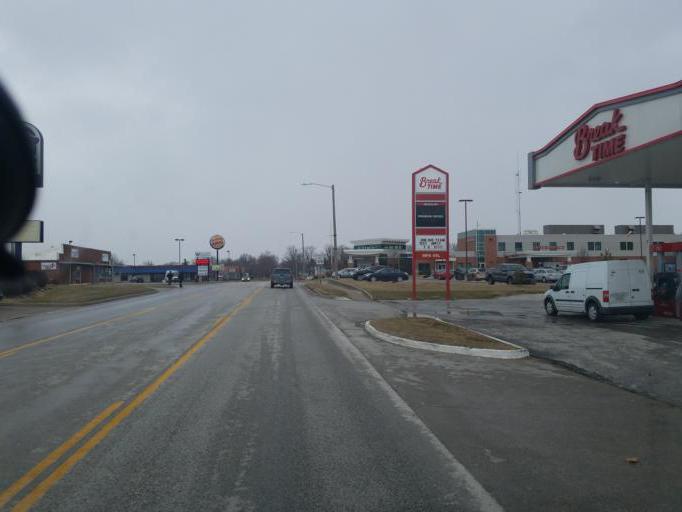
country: US
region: Missouri
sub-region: Macon County
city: Macon
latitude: 39.7492
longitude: -92.4679
